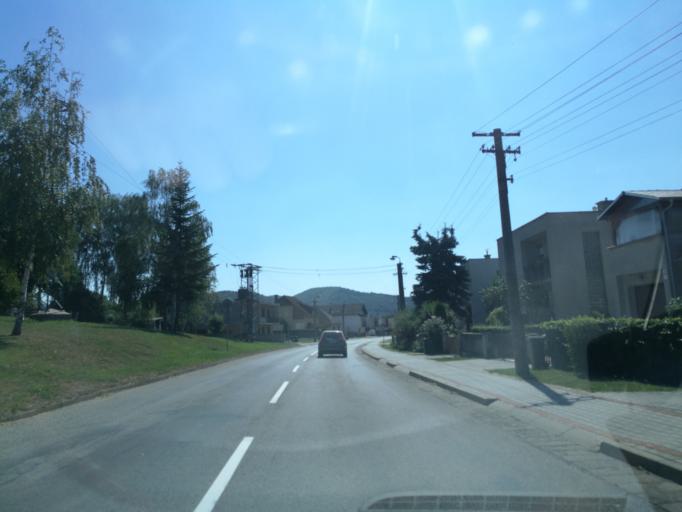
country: SK
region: Nitriansky
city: Brezova pod Bradlom
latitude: 48.6736
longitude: 17.5374
